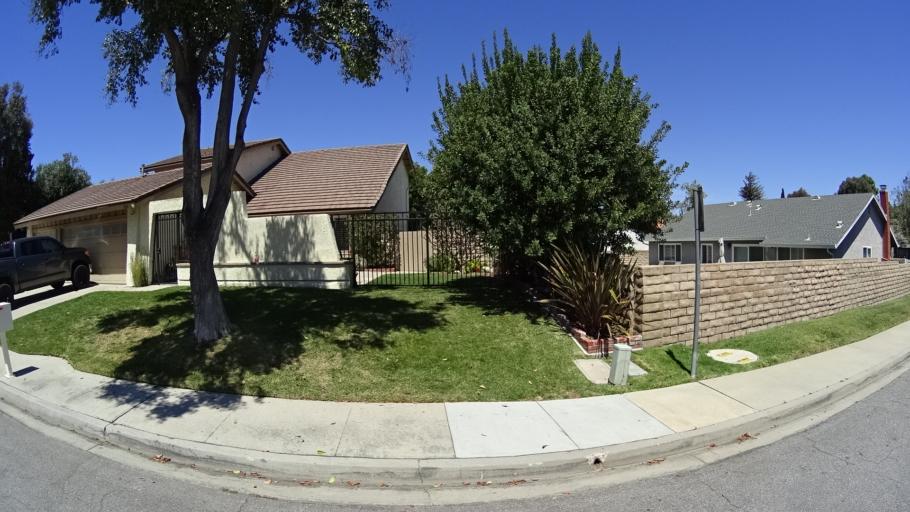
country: US
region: California
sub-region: Ventura County
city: Casa Conejo
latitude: 34.1790
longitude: -118.8959
